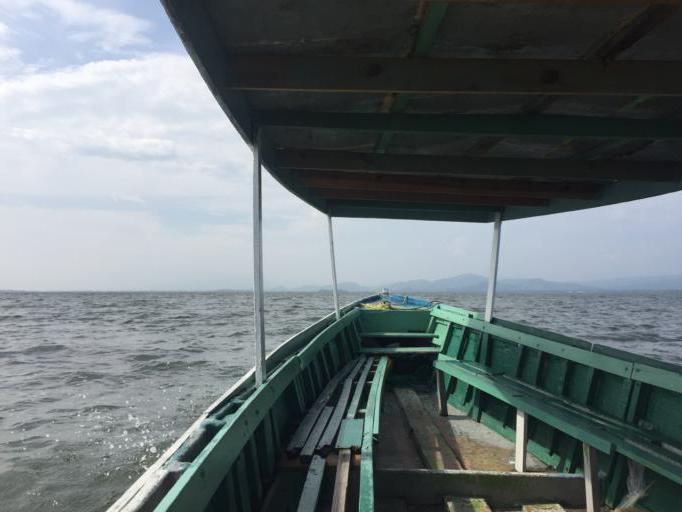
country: MX
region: Guerrero
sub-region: Coyuca de Benitez
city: Colonia Luces en el Mar
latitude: 16.9182
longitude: -99.9832
